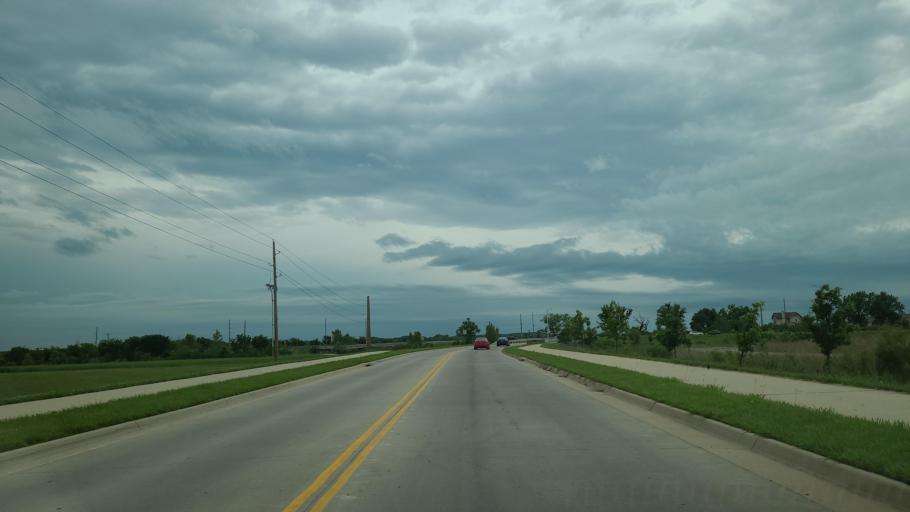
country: US
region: Kansas
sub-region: Douglas County
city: Lawrence
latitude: 38.9300
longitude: -95.2418
